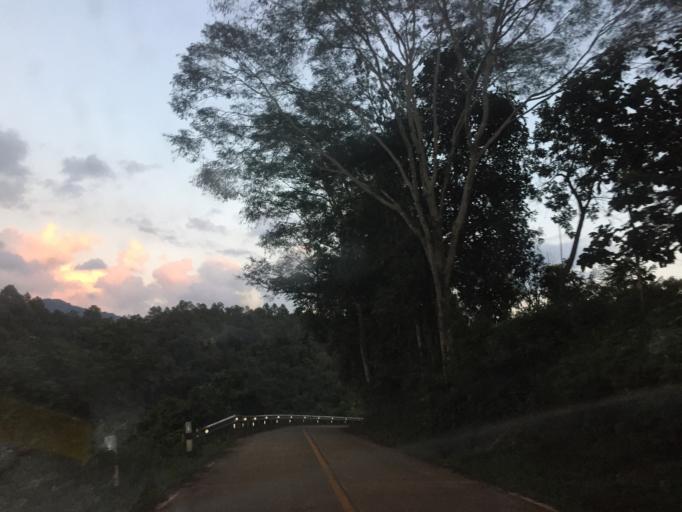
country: TH
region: Chiang Mai
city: Samoeng
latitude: 18.9990
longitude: 98.7157
